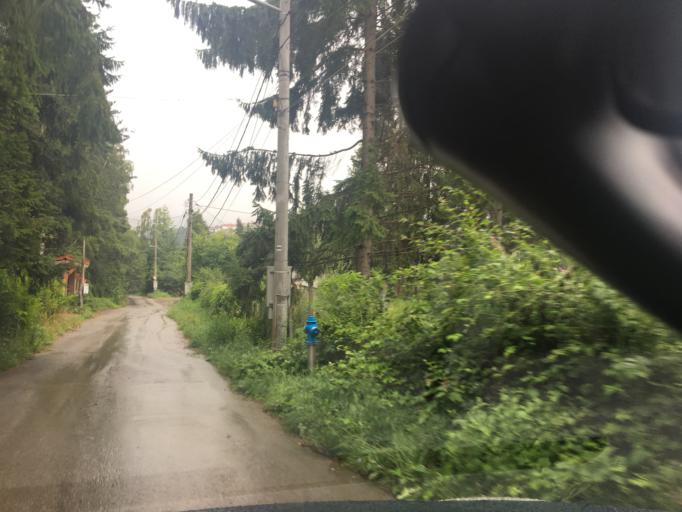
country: BG
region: Sofia-Capital
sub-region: Stolichna Obshtina
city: Sofia
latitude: 42.5861
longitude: 23.3427
